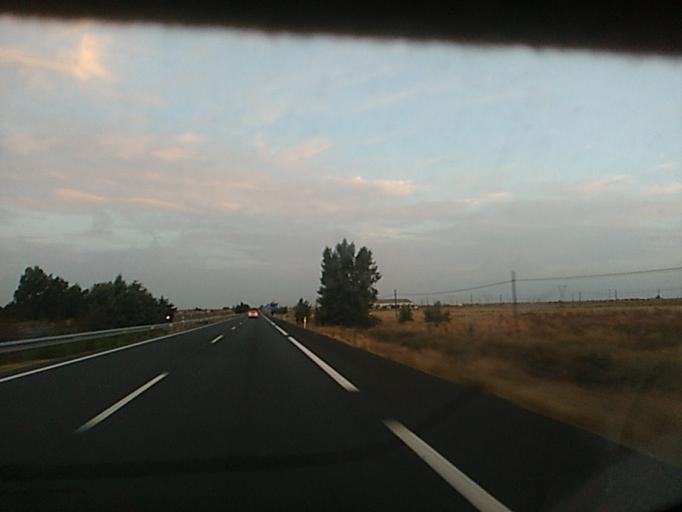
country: ES
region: Castille and Leon
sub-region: Provincia de Segovia
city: Martin Munoz de la Dehesa
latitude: 41.0321
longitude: -4.6882
